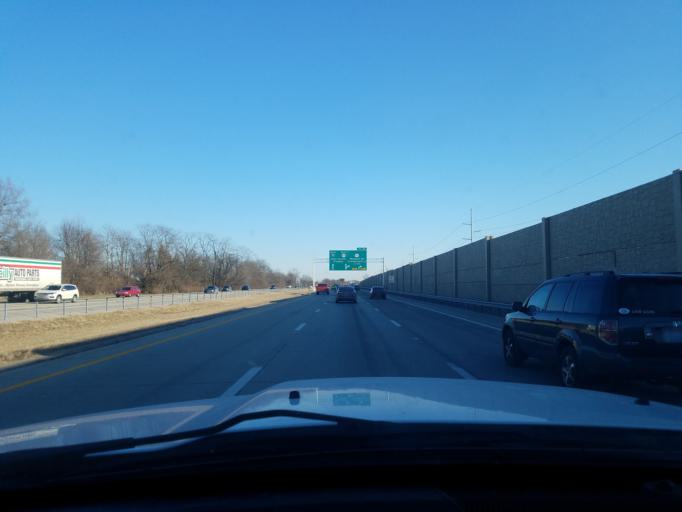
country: US
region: Kentucky
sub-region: Jefferson County
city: Worthington
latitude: 38.3058
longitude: -85.5651
